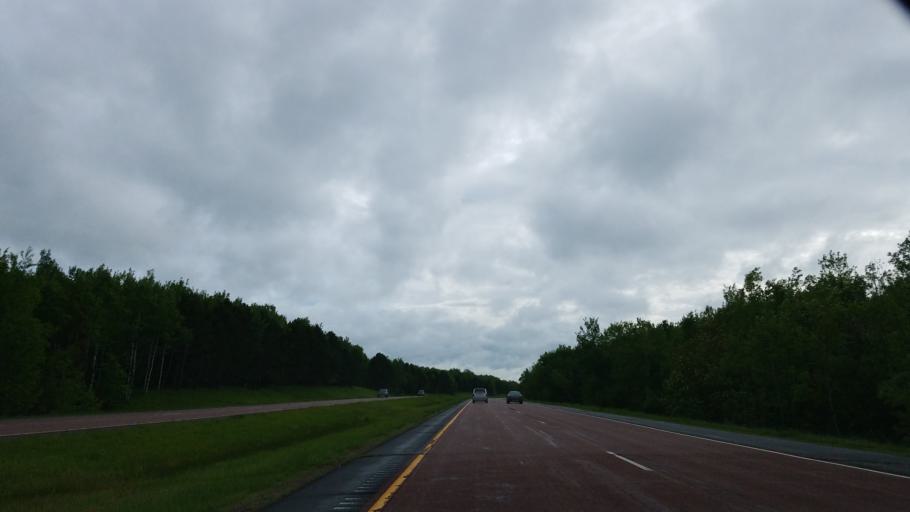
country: US
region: Minnesota
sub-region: Saint Louis County
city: Arnold
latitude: 46.8578
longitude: -91.9802
